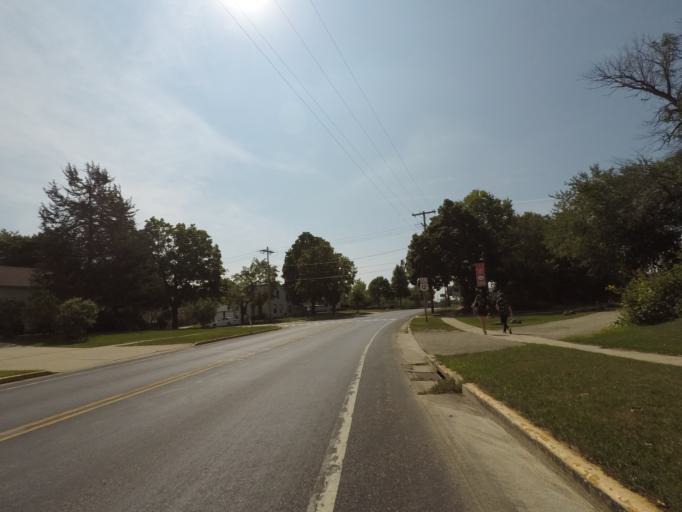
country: US
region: Wisconsin
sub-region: Jefferson County
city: Fort Atkinson
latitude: 42.9329
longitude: -88.8373
